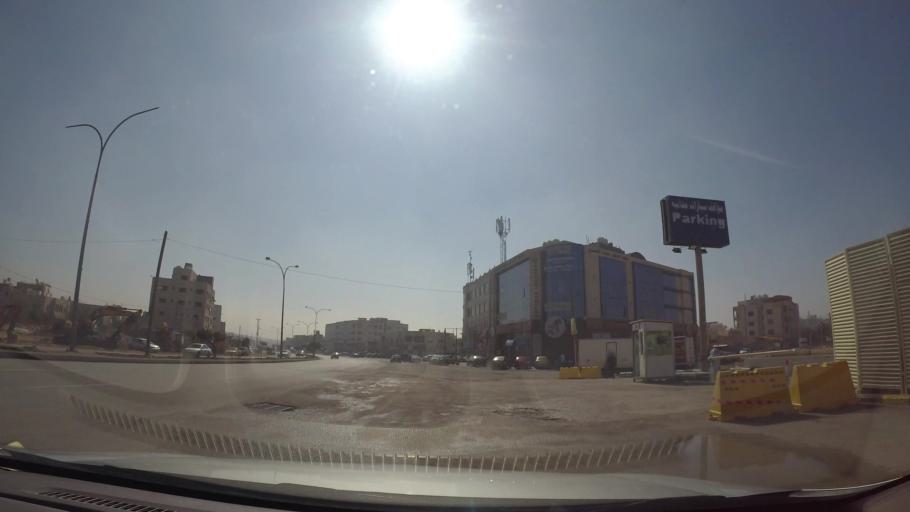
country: JO
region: Amman
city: Al Bunayyat ash Shamaliyah
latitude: 31.9034
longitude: 35.8884
